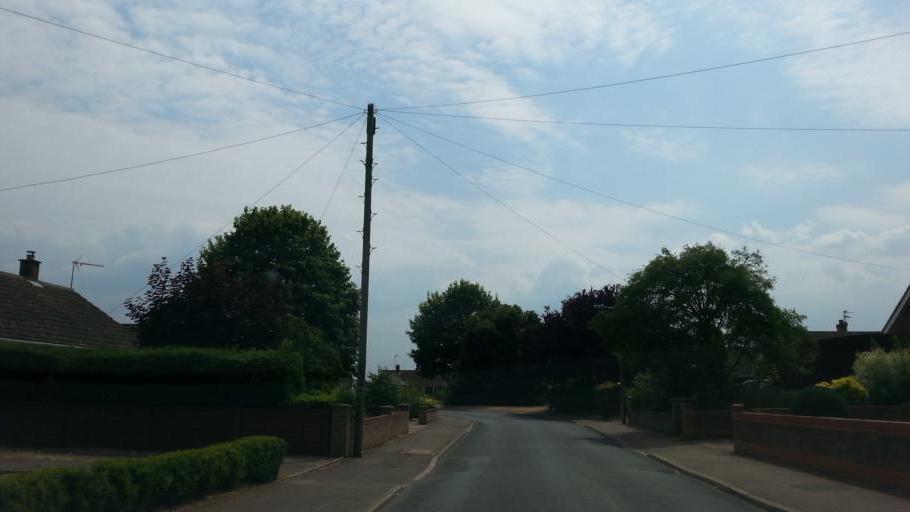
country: GB
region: England
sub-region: Suffolk
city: Lakenheath
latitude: 52.4168
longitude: 0.5286
